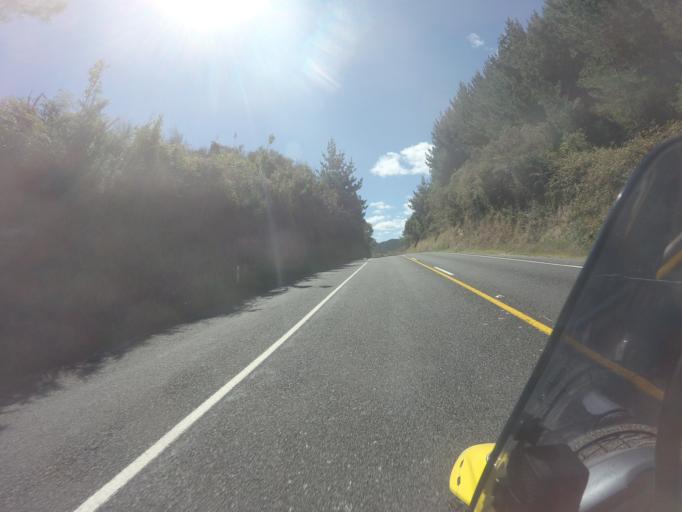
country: NZ
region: Bay of Plenty
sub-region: Whakatane District
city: Murupara
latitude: -38.3083
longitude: 176.8098
